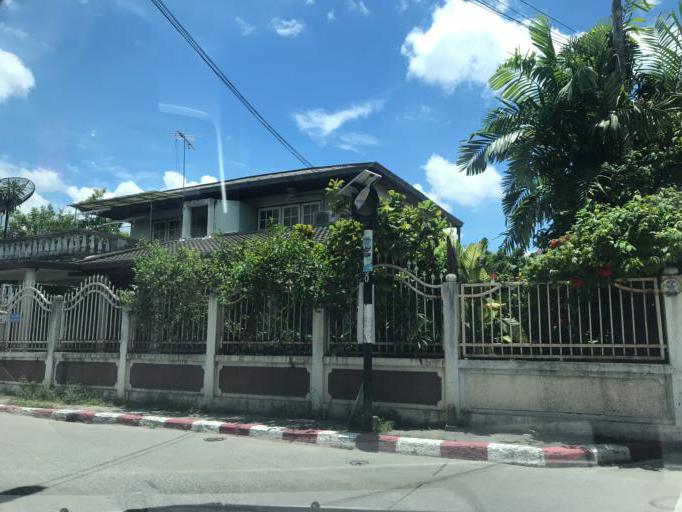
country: TH
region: Chiang Mai
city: Chiang Mai
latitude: 18.7755
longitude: 98.9871
